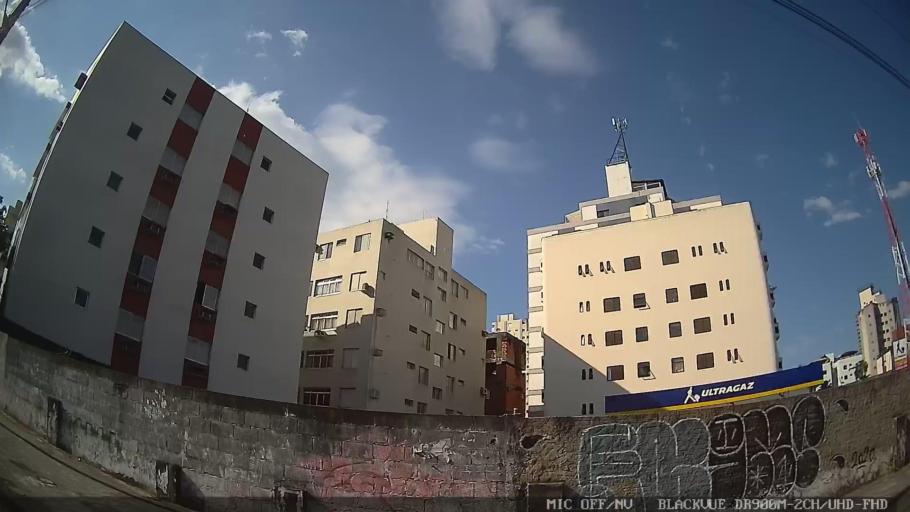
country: BR
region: Sao Paulo
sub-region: Guaruja
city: Guaruja
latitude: -23.9784
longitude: -46.2240
